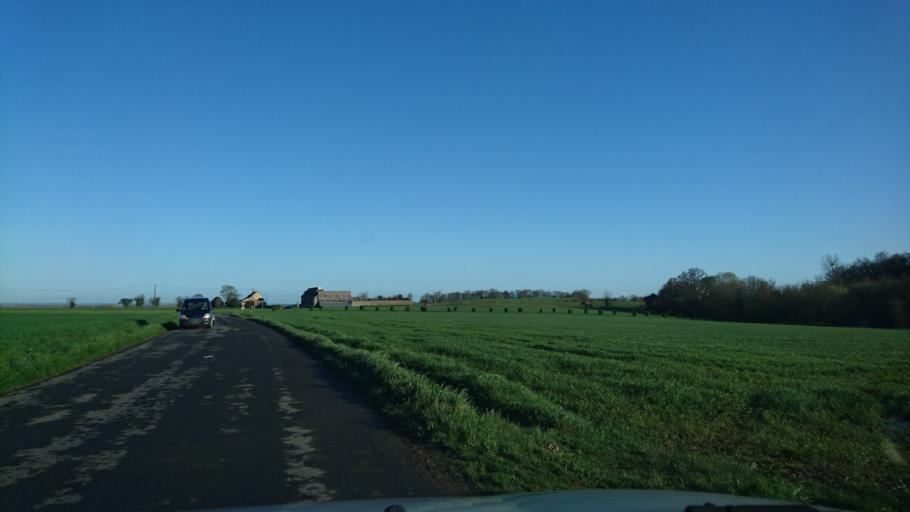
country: FR
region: Brittany
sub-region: Departement d'Ille-et-Vilaine
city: Baguer-Pican
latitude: 48.5607
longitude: -1.7051
